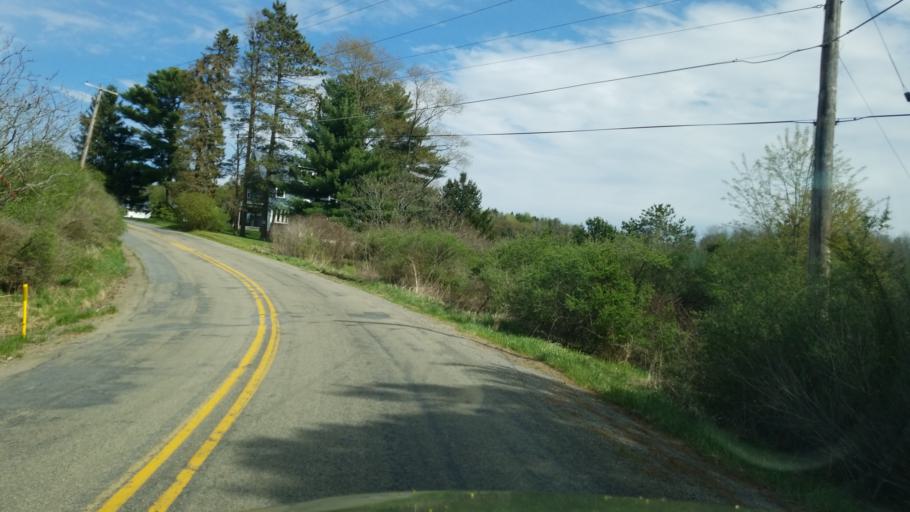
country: US
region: Pennsylvania
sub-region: Jefferson County
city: Brockway
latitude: 41.2213
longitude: -78.8478
